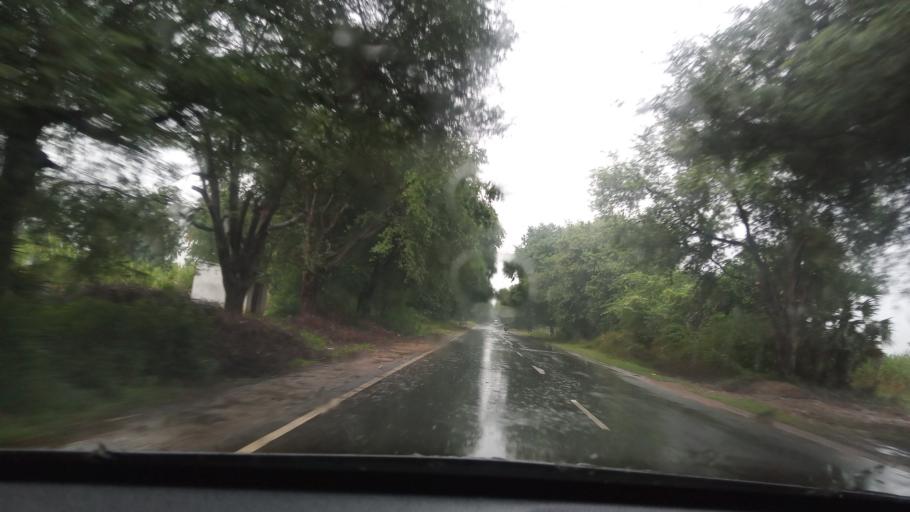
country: IN
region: Tamil Nadu
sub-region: Vellore
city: Kalavai
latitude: 12.8458
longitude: 79.3953
